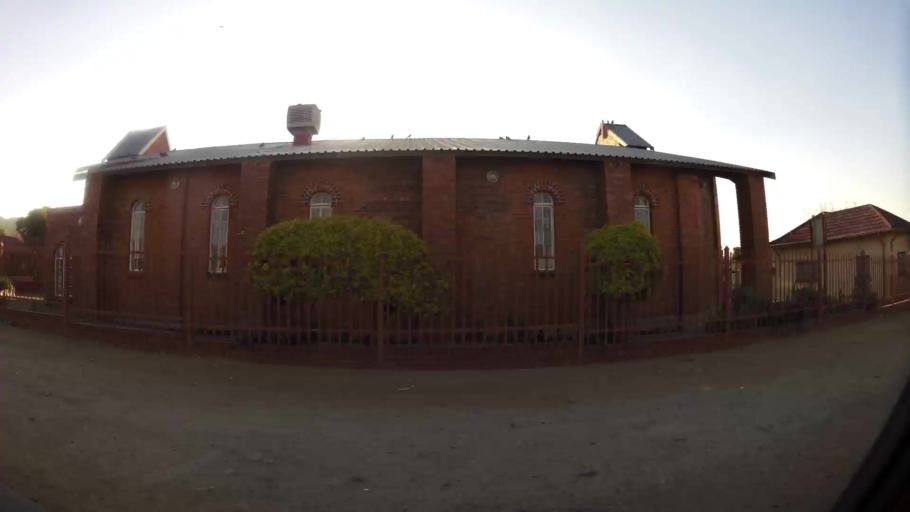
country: ZA
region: North-West
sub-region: Bojanala Platinum District Municipality
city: Rustenburg
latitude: -25.6461
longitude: 27.2176
